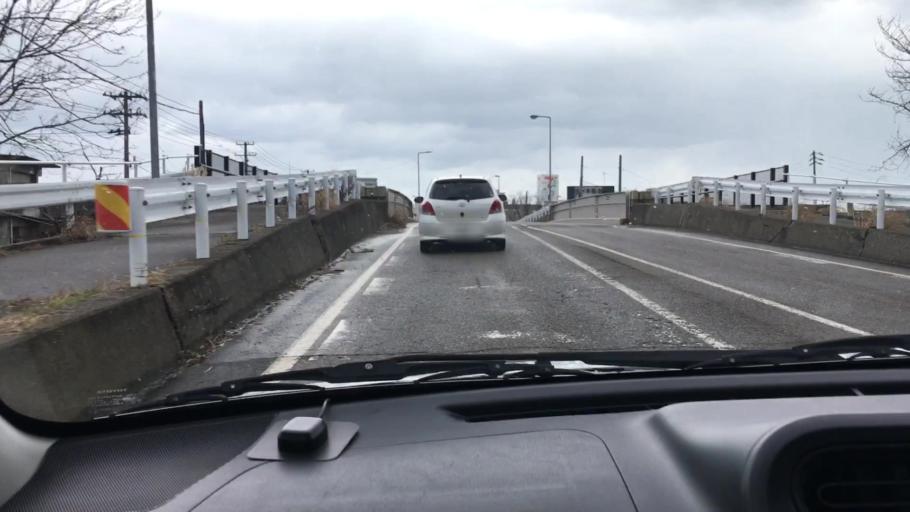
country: JP
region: Niigata
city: Joetsu
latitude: 37.1669
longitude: 138.2370
